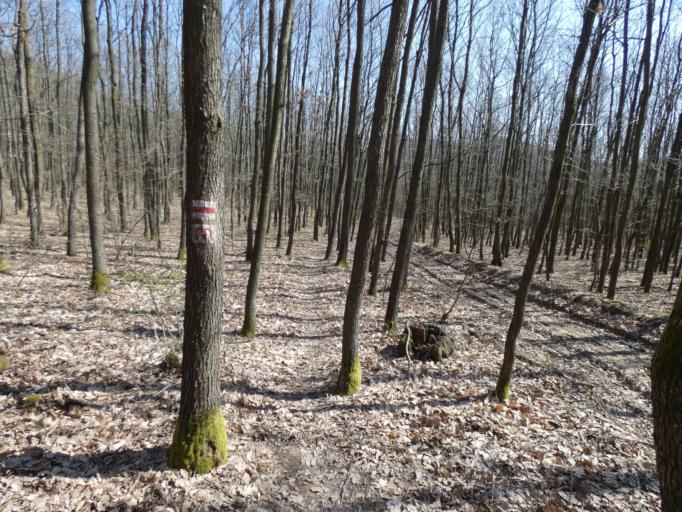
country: HU
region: Pest
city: Szob
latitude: 47.8695
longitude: 18.9122
